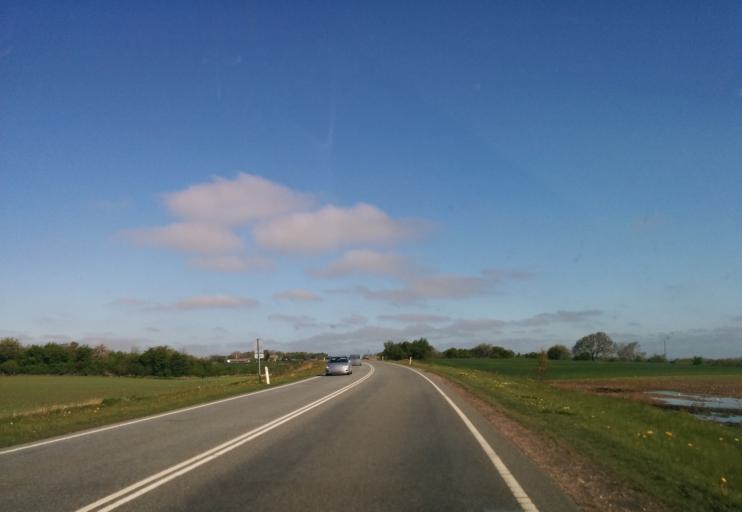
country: DK
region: Central Jutland
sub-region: Arhus Kommune
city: Stavtrup
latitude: 56.1142
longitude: 10.1134
